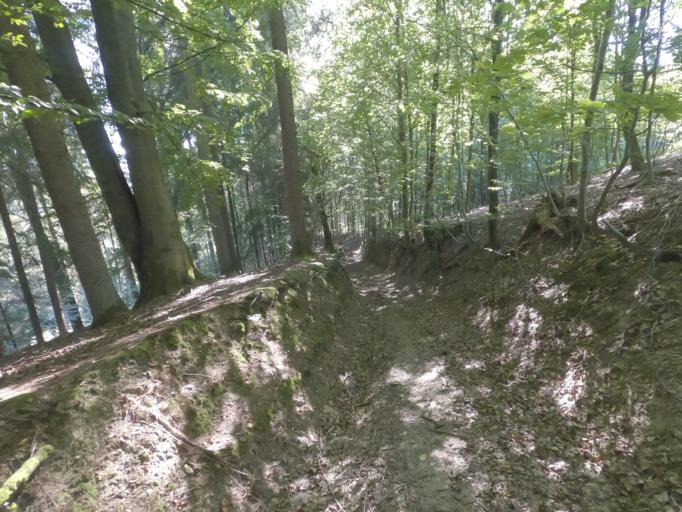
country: DE
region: Bavaria
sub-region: Lower Bavaria
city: Deggendorf
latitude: 48.8217
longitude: 13.0098
